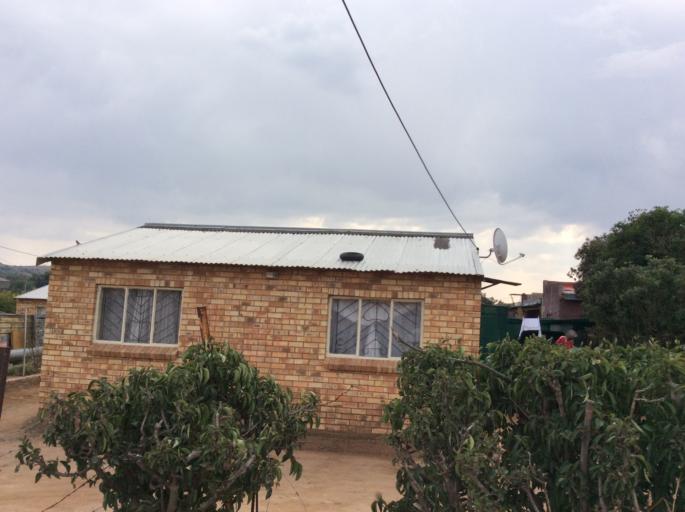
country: ZA
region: Orange Free State
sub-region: Xhariep District Municipality
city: Dewetsdorp
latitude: -29.5803
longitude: 26.6799
